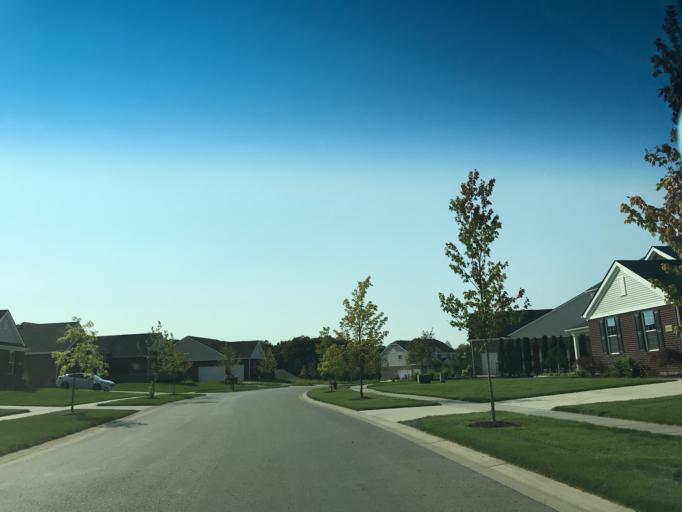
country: US
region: Michigan
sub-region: Oakland County
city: South Lyon
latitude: 42.4839
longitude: -83.6619
